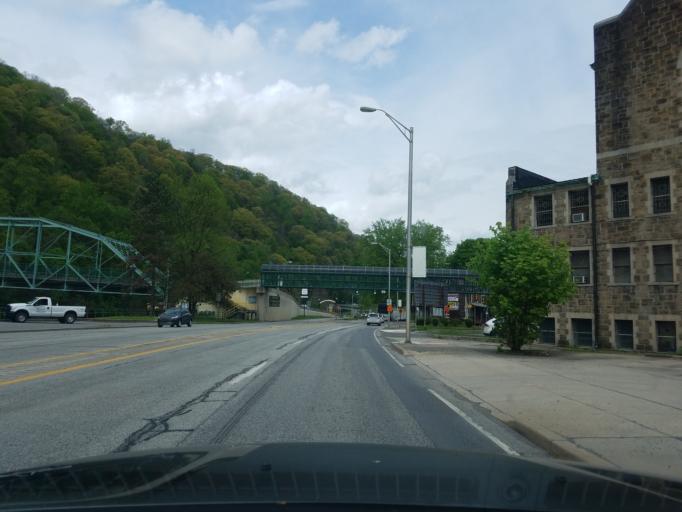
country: US
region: Pennsylvania
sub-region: Cambria County
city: Johnstown
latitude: 40.3253
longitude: -78.9245
